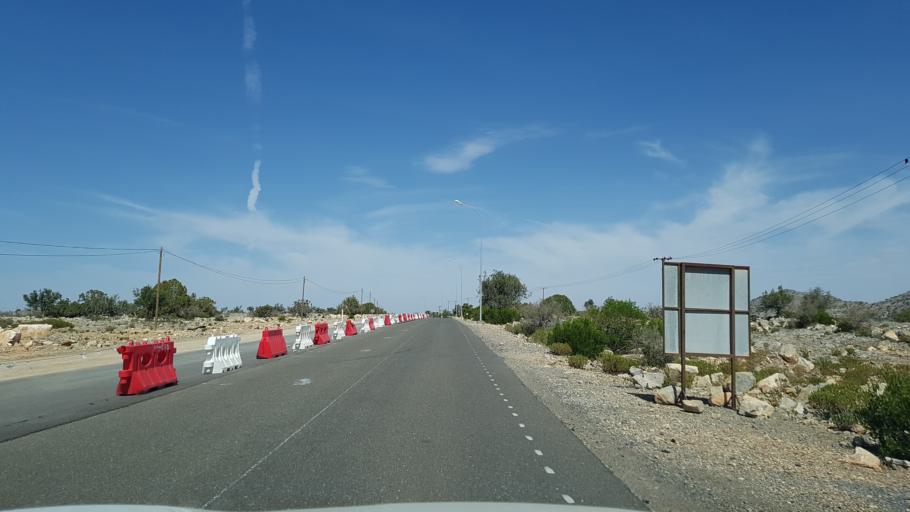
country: OM
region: Muhafazat ad Dakhiliyah
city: Nizwa
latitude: 23.1181
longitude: 57.6277
